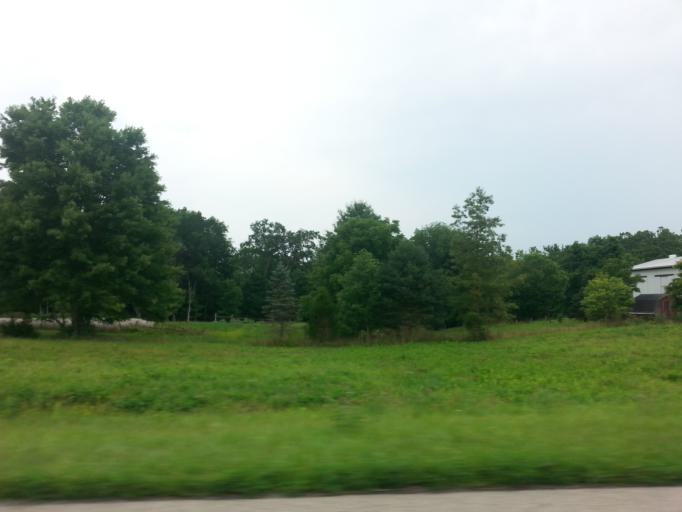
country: US
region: Ohio
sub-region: Brown County
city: Ripley
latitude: 38.8128
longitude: -83.8050
